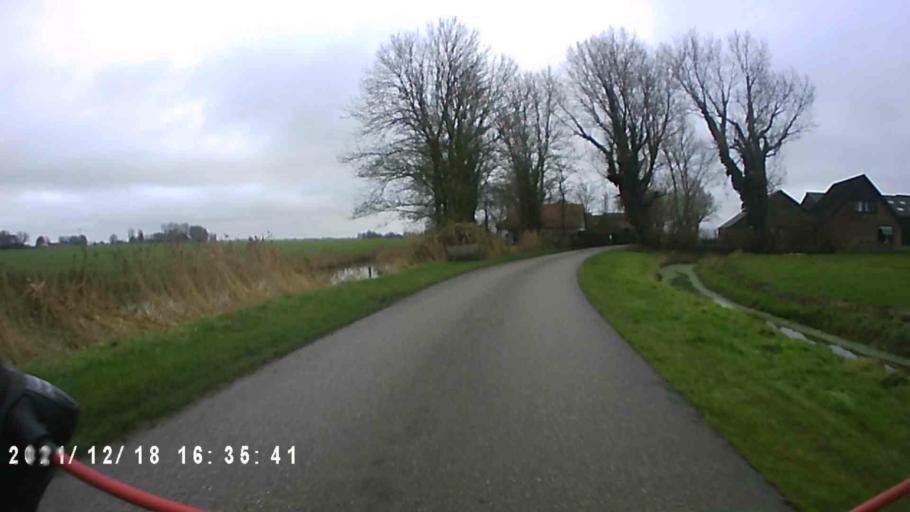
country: NL
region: Friesland
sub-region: Gemeente Dongeradeel
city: Dokkum
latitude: 53.3564
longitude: 6.0213
